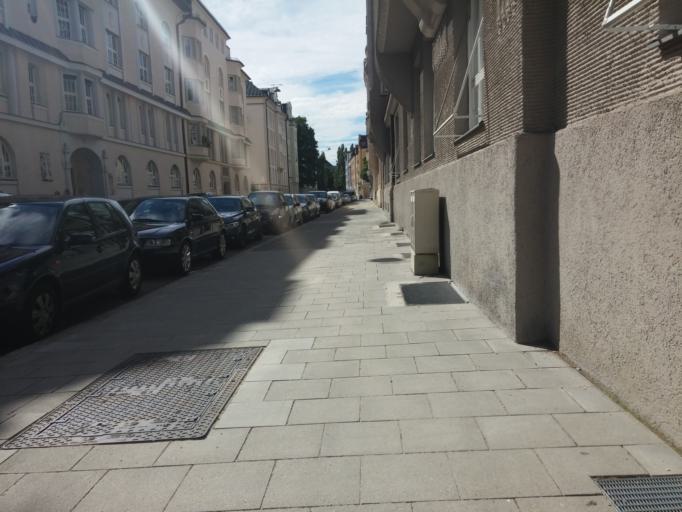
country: DE
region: Bavaria
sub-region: Upper Bavaria
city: Munich
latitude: 48.1534
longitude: 11.5875
